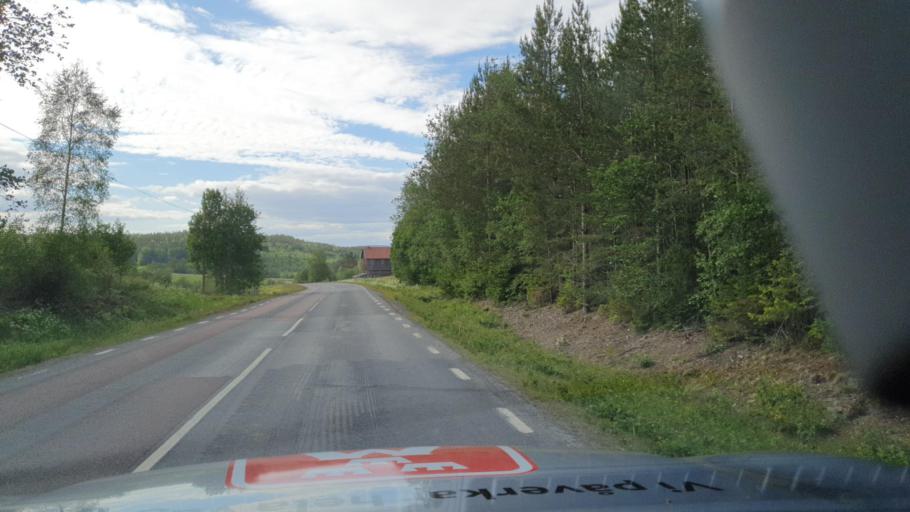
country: SE
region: Vaesternorrland
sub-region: Kramfors Kommun
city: Nordingra
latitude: 62.8680
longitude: 18.1576
